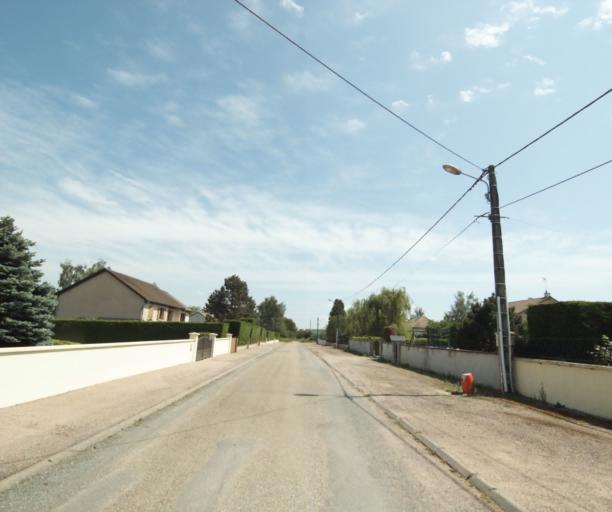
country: FR
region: Bourgogne
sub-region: Departement de Saone-et-Loire
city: Gueugnon
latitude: 46.5767
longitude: 4.1396
